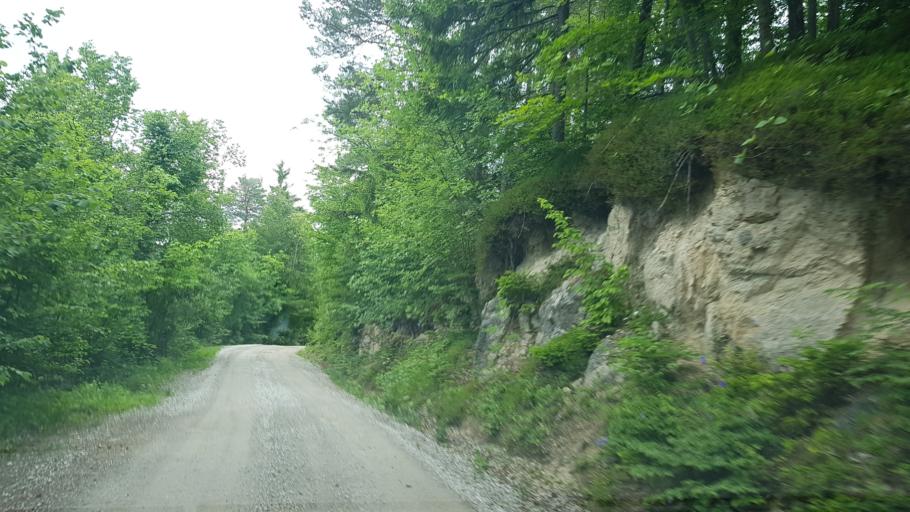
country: SI
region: Dobrna
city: Dobrna
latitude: 46.3602
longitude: 15.2478
